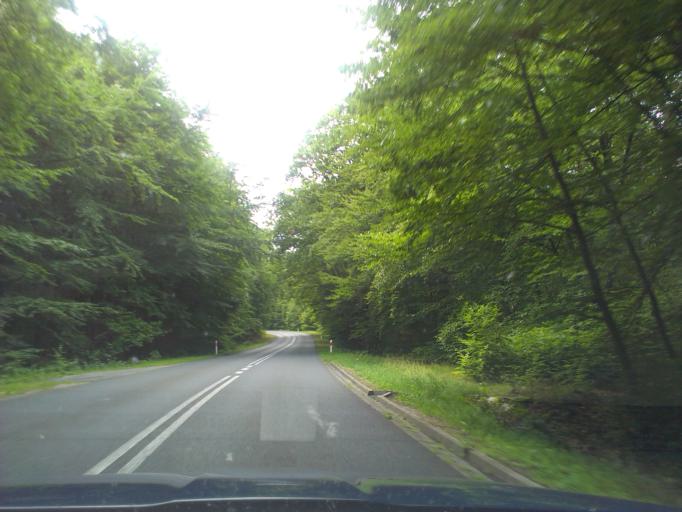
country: PL
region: West Pomeranian Voivodeship
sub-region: Powiat kamienski
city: Miedzyzdroje
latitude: 53.9424
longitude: 14.4838
